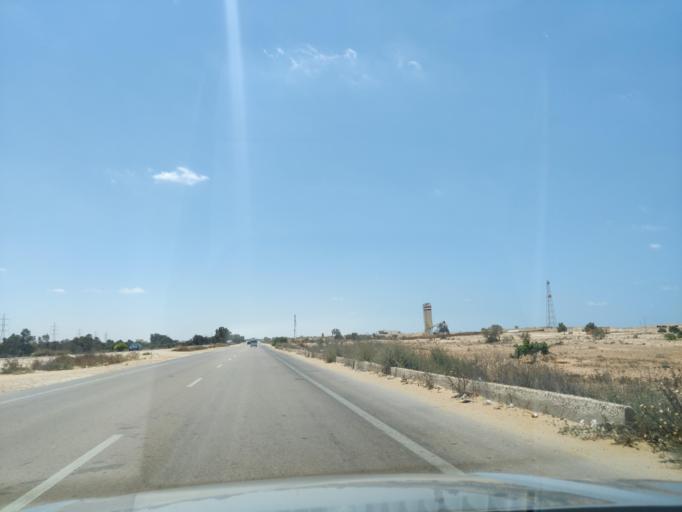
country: EG
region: Muhafazat Matruh
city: Al `Alamayn
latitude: 31.0699
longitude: 28.1461
